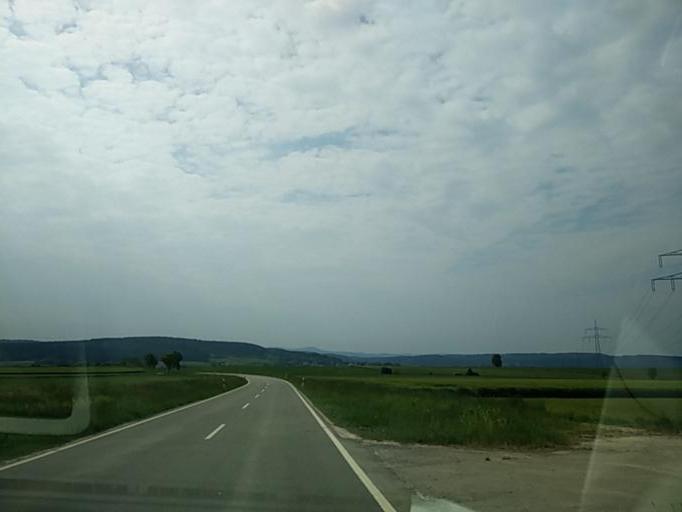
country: DE
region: Baden-Wuerttemberg
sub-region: Tuebingen Region
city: Hirrlingen
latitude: 48.4232
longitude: 8.8815
